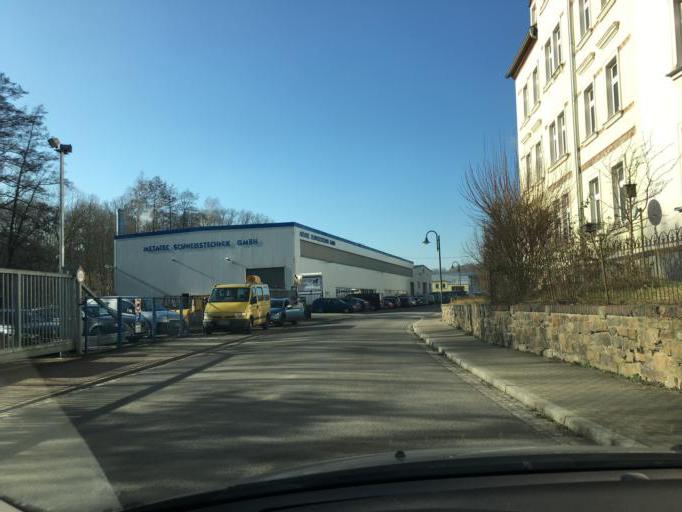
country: DE
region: Saxony
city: Penig
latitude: 50.9320
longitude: 12.7003
